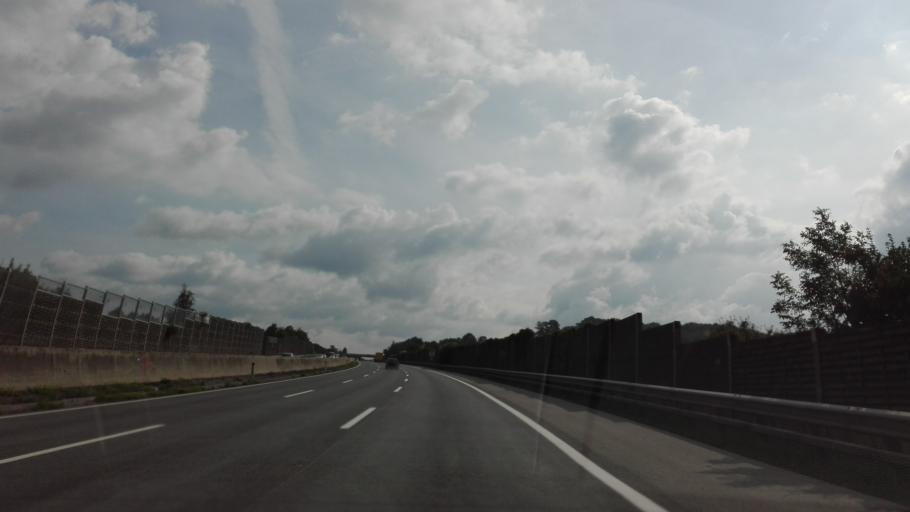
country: AT
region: Lower Austria
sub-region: Politischer Bezirk Melk
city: Melk
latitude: 48.2145
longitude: 15.3137
